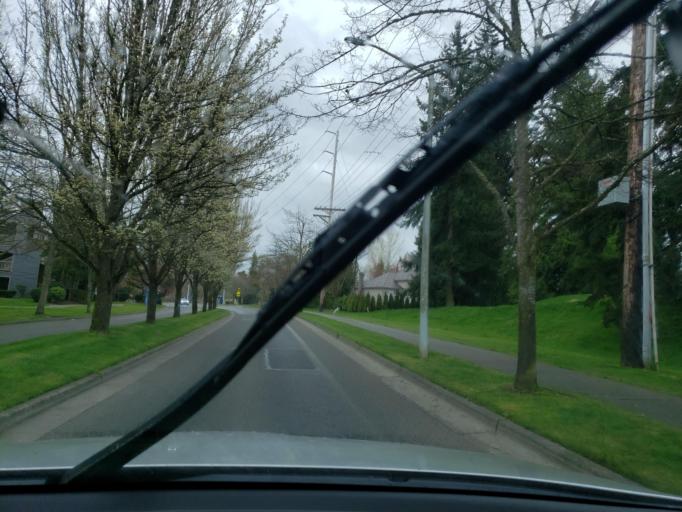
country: US
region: Washington
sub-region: Snohomish County
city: Meadowdale
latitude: 47.8887
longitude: -122.3111
